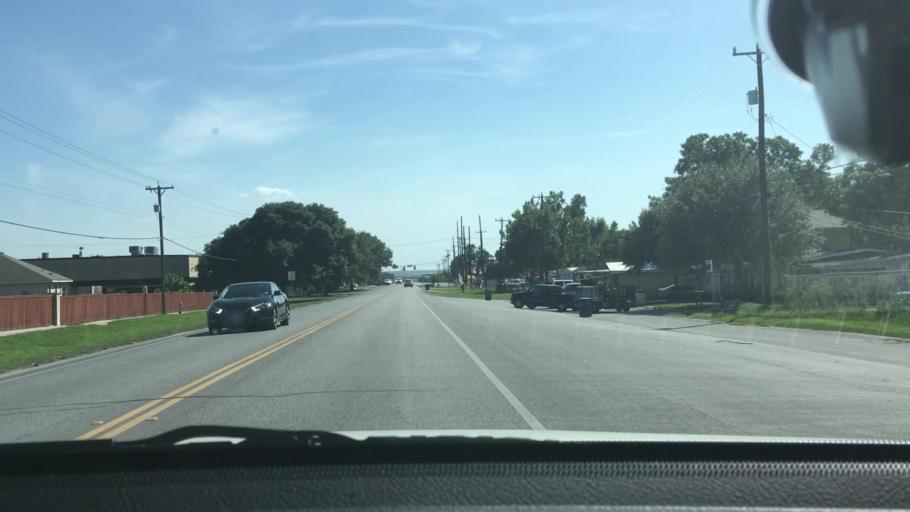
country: US
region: Texas
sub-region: Bexar County
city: Windcrest
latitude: 29.5347
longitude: -98.3771
